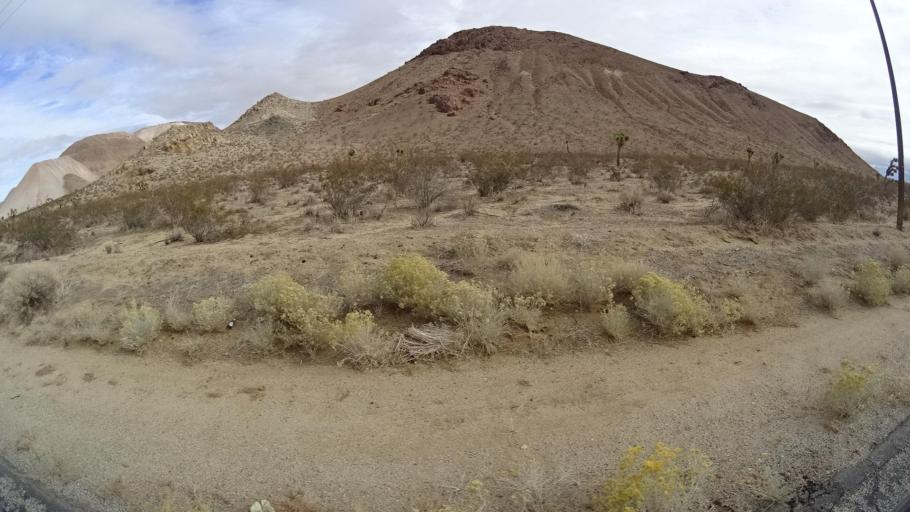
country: US
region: California
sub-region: Kern County
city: Mojave
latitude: 34.9641
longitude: -118.2128
